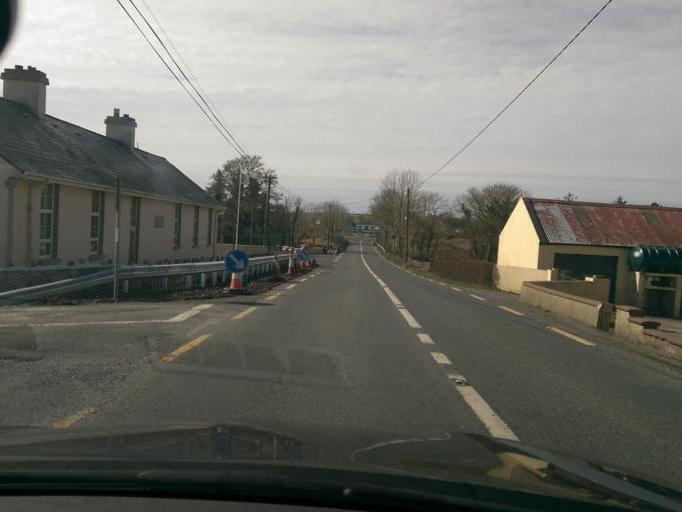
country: IE
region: Connaught
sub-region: County Galway
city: Athenry
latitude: 53.4662
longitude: -8.6631
